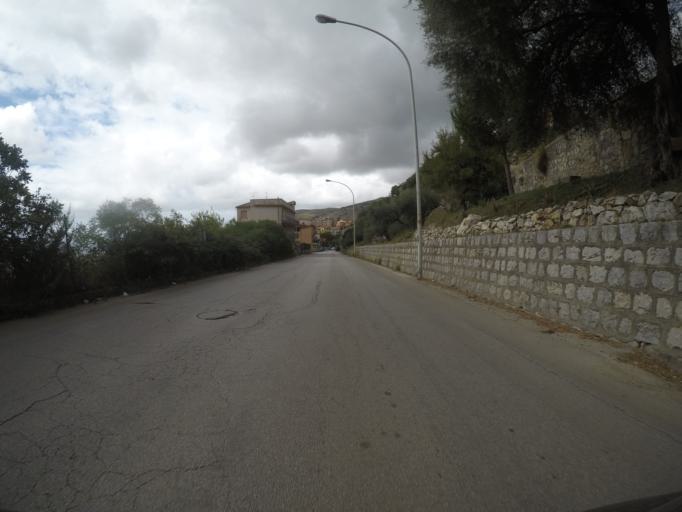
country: IT
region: Sicily
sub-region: Palermo
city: Montelepre
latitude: 38.0920
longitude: 13.1768
